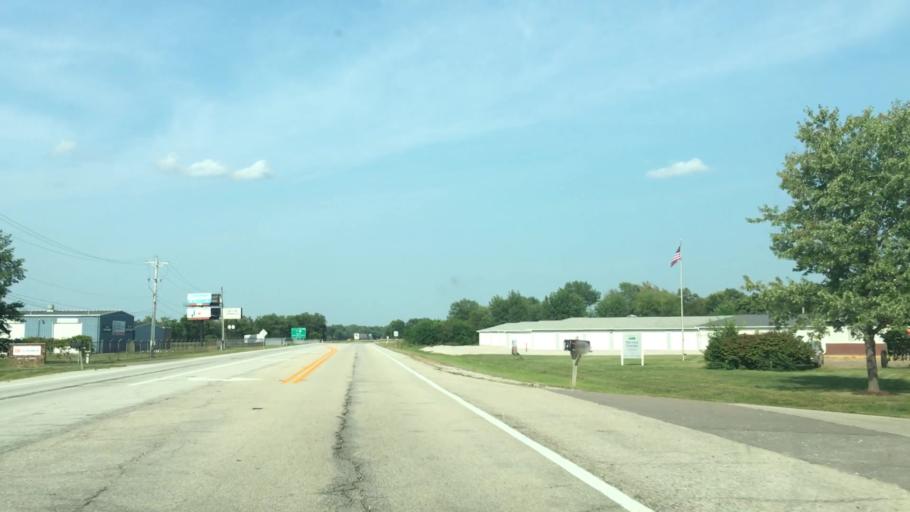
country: US
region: Illinois
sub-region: Rock Island County
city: Milan
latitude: 41.4541
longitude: -90.5265
